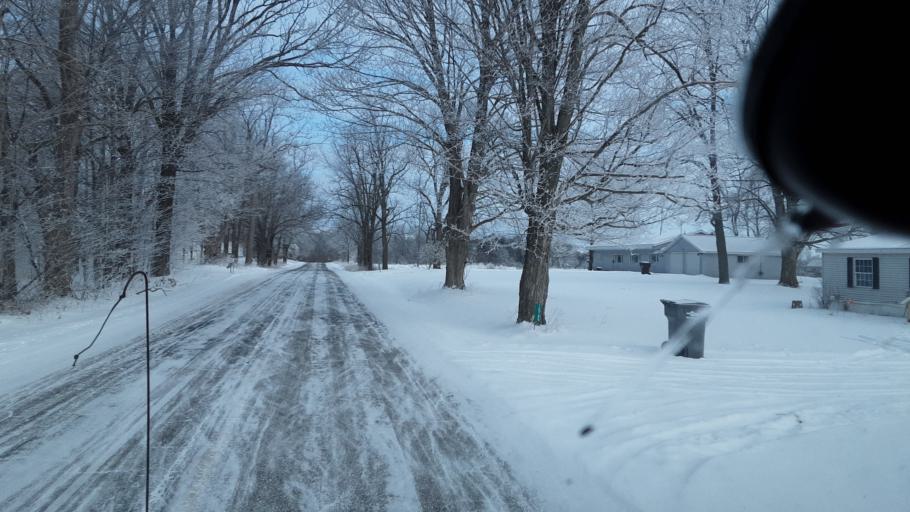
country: US
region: Michigan
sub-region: Ingham County
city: Leslie
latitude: 42.3891
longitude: -84.4924
